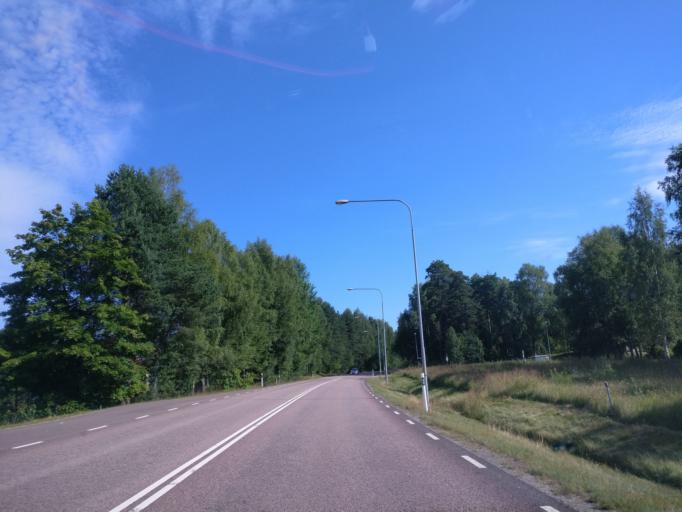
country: SE
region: Vaermland
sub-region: Hagfors Kommun
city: Hagfors
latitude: 60.0545
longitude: 13.7050
